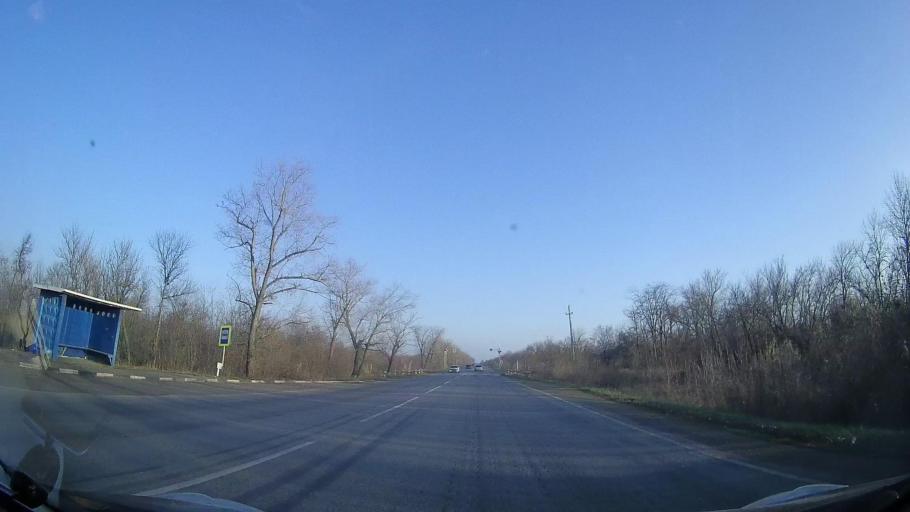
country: RU
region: Rostov
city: Bataysk
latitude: 47.0739
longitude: 39.7890
